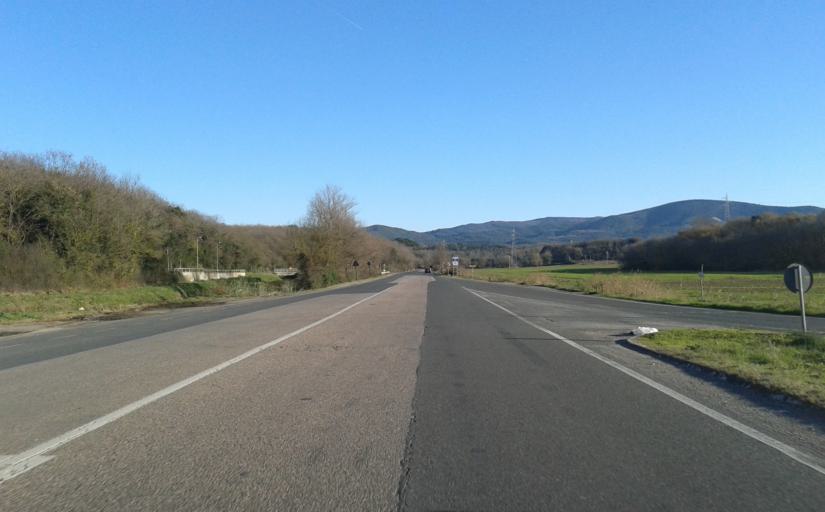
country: IT
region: Tuscany
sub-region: Provincia di Livorno
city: Livorno
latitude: 43.5718
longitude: 10.3519
